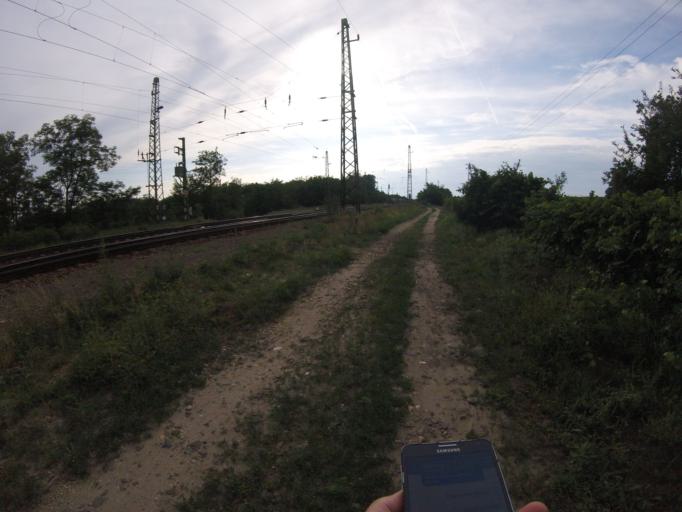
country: HU
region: Pest
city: Cegledbercel
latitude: 47.2081
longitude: 19.6938
